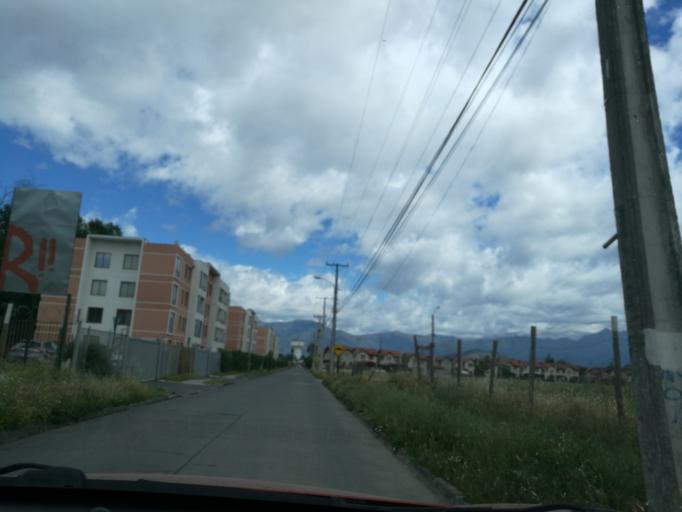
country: CL
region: O'Higgins
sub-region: Provincia de Cachapoal
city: Rancagua
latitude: -34.1443
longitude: -70.7312
